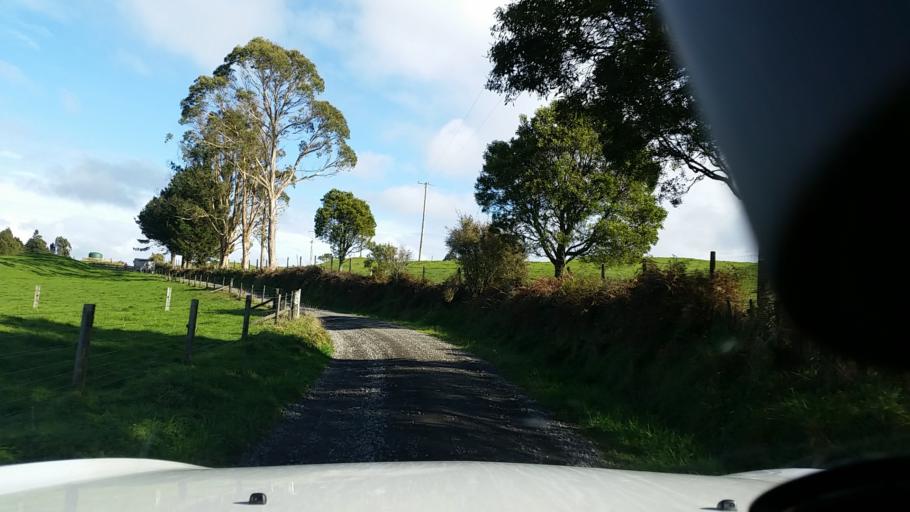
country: NZ
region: Bay of Plenty
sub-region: Rotorua District
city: Rotorua
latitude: -37.9863
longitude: 176.1660
